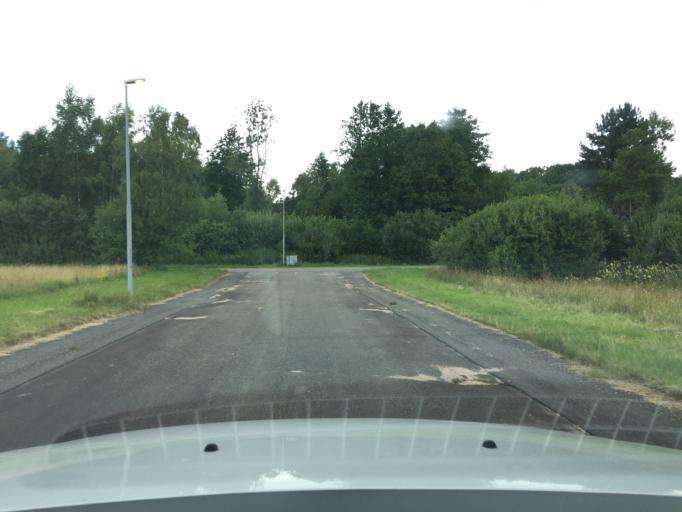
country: SE
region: Skane
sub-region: Hassleholms Kommun
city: Sosdala
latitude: 56.0454
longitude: 13.6724
